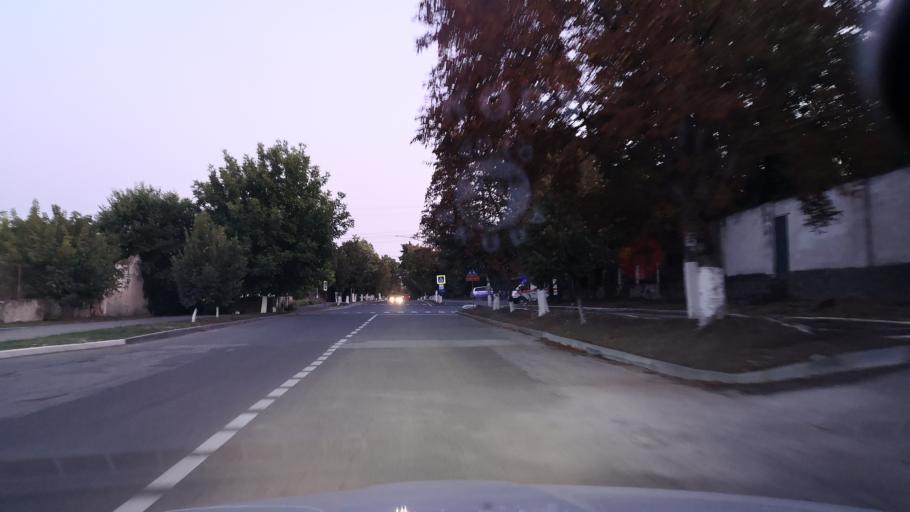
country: MD
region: Orhei
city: Orhei
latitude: 47.3894
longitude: 28.8237
